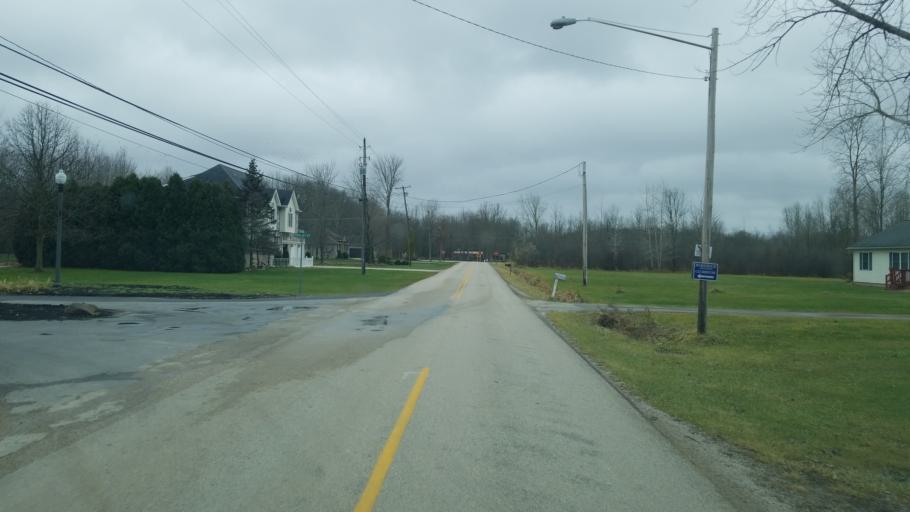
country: US
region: Ohio
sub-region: Ashtabula County
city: Roaming Shores
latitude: 41.6371
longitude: -80.8360
